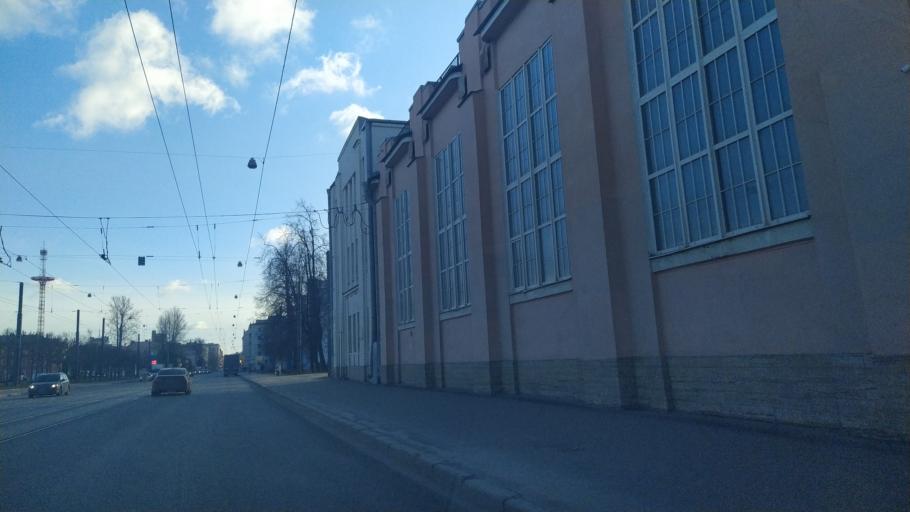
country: RU
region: Leningrad
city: Finlyandskiy
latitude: 59.9698
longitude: 30.3488
